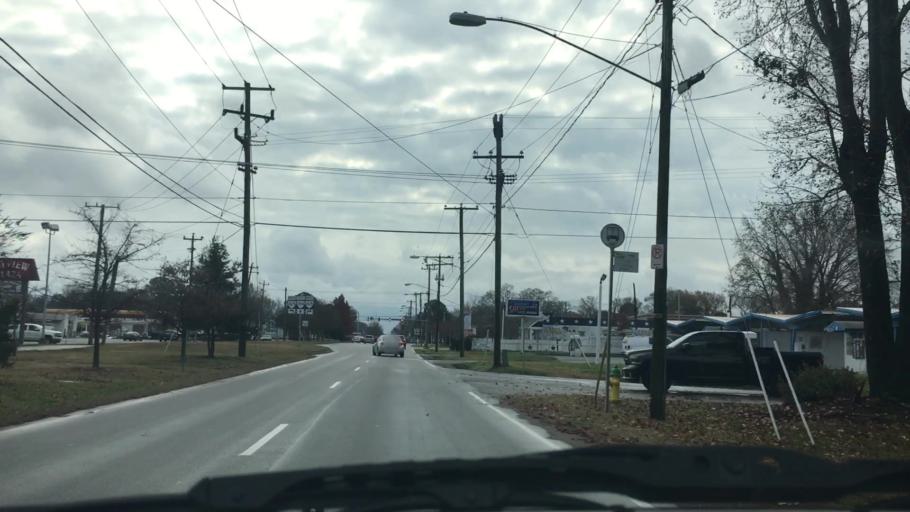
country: US
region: Virginia
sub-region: City of Norfolk
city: Norfolk
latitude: 36.9168
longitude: -76.2420
